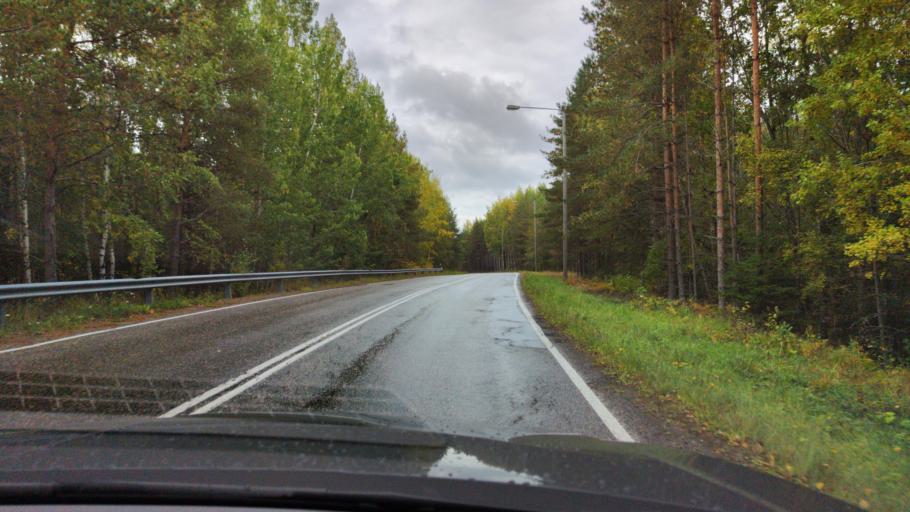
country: FI
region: Varsinais-Suomi
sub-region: Turku
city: Turku
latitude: 60.3672
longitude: 22.2172
